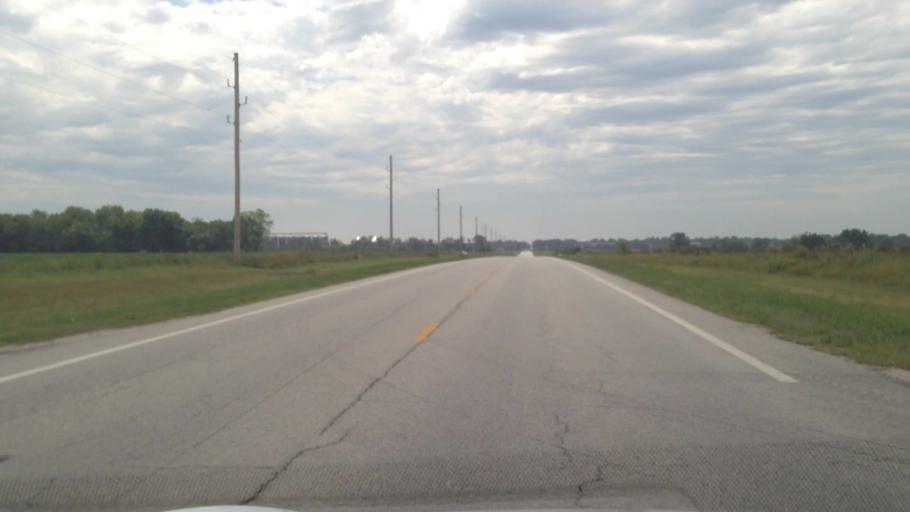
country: US
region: Kansas
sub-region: Allen County
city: Iola
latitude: 37.9360
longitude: -95.1701
